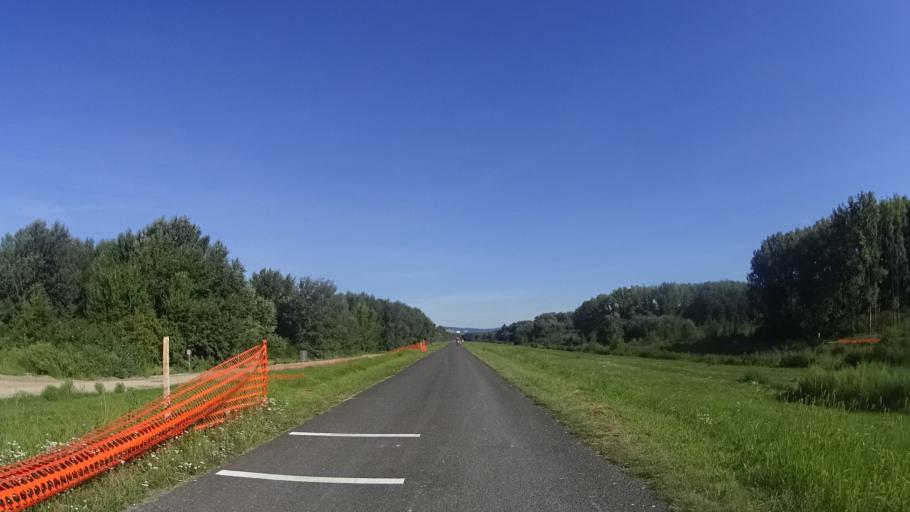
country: SK
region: Bratislavsky
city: Bratislava
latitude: 48.0845
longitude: 17.1575
